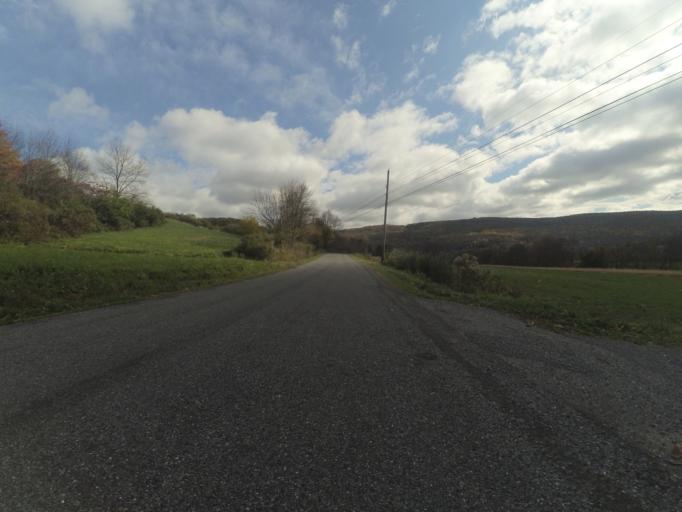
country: US
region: Pennsylvania
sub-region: Centre County
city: Park Forest Village
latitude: 40.9007
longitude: -77.9005
